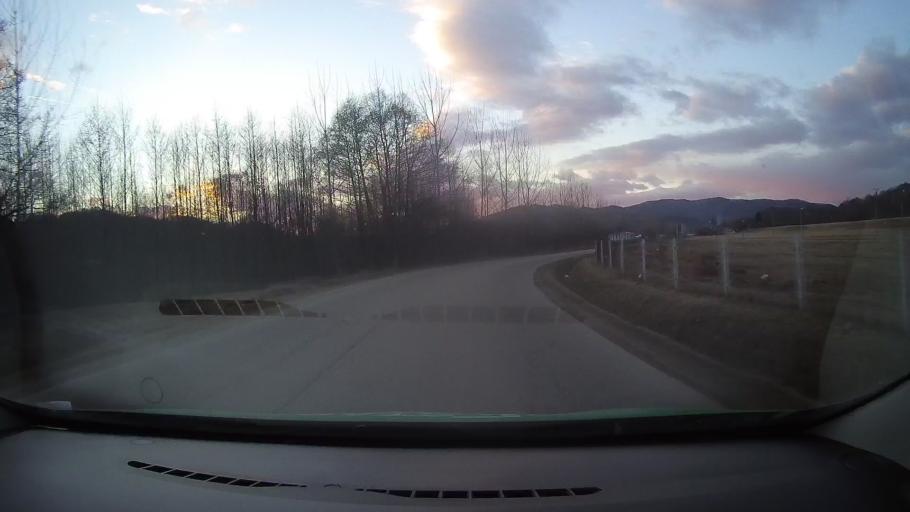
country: RO
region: Dambovita
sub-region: Comuna Valea Lunga
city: Valea Lunga Ogrea
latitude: 45.0613
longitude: 25.5911
